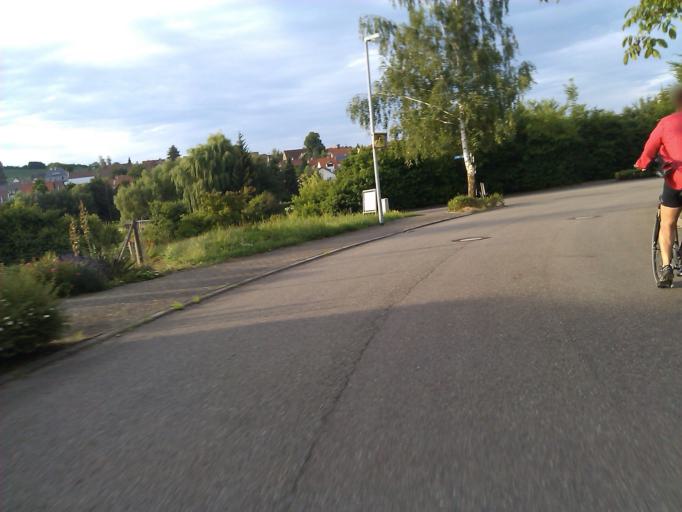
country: DE
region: Baden-Wuerttemberg
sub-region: Regierungsbezirk Stuttgart
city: Guglingen
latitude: 49.0630
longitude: 8.9950
